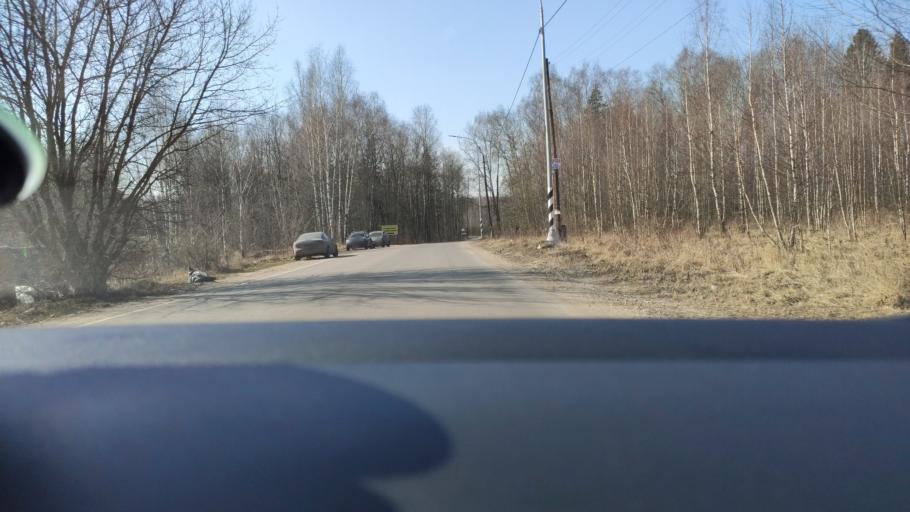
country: RU
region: Moskovskaya
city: Elektrostal'
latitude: 55.7729
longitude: 38.4135
